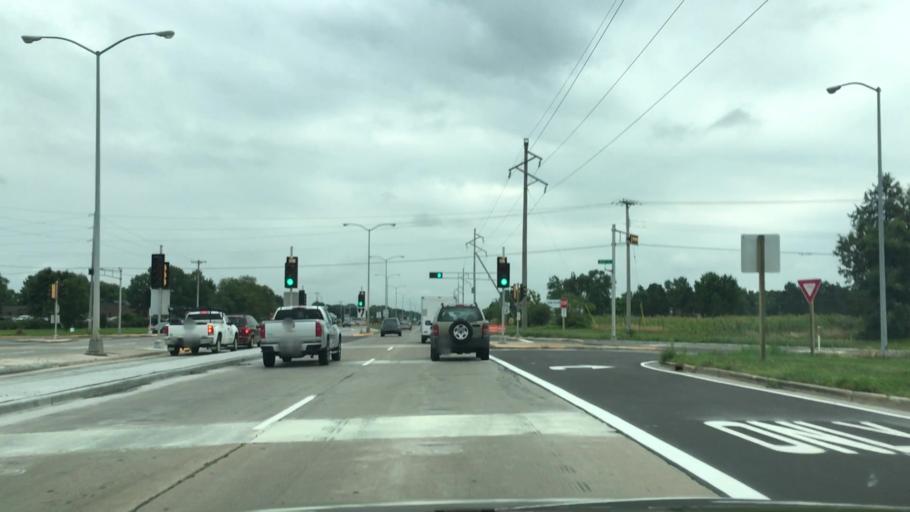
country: US
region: Wisconsin
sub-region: Eau Claire County
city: Eau Claire
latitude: 44.8200
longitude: -91.5435
